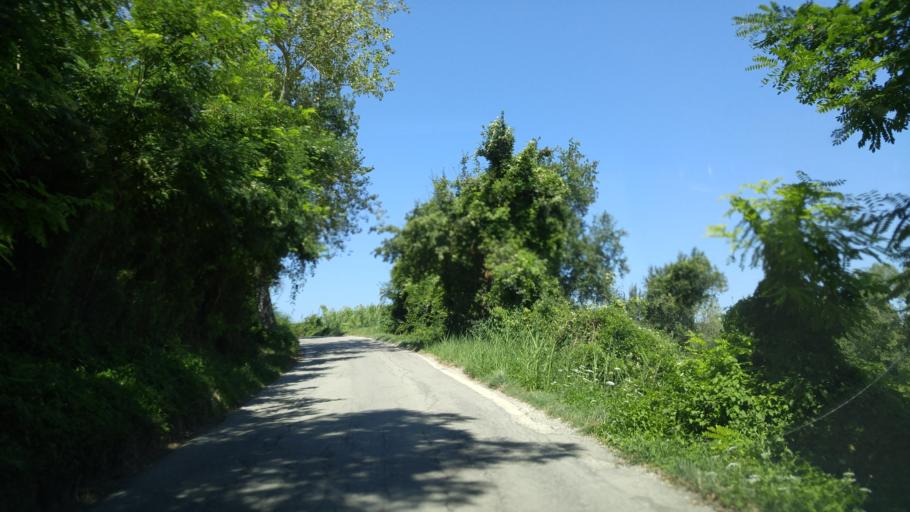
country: IT
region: The Marches
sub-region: Provincia di Pesaro e Urbino
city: Fenile
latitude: 43.8351
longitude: 12.9702
